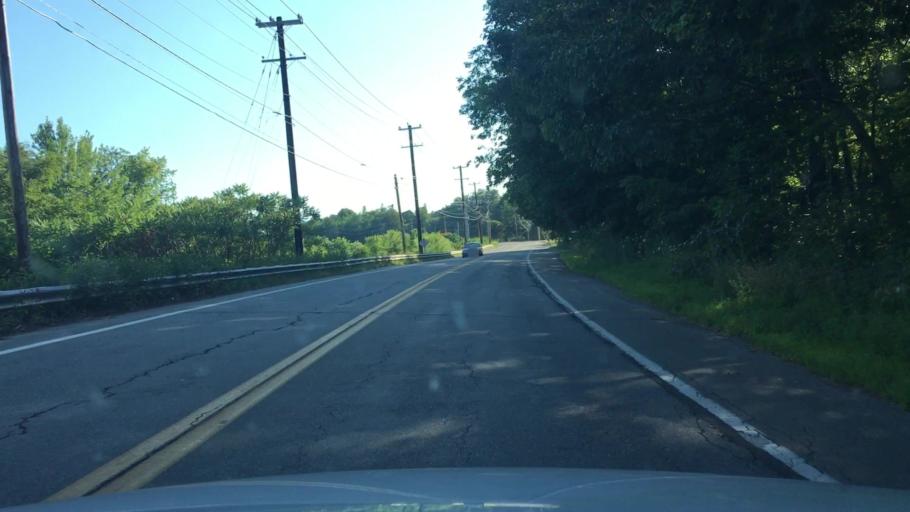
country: US
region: Maine
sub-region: Penobscot County
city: Brewer
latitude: 44.8163
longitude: -68.7332
